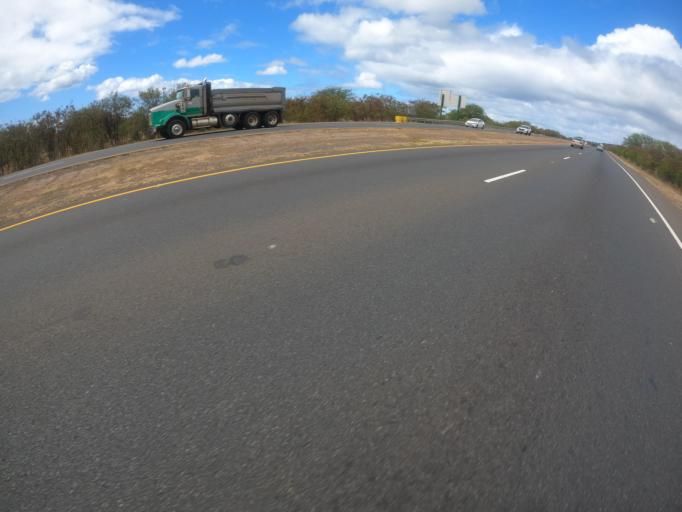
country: US
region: Hawaii
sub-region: Honolulu County
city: Makakilo City
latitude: 21.3370
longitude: -158.0967
